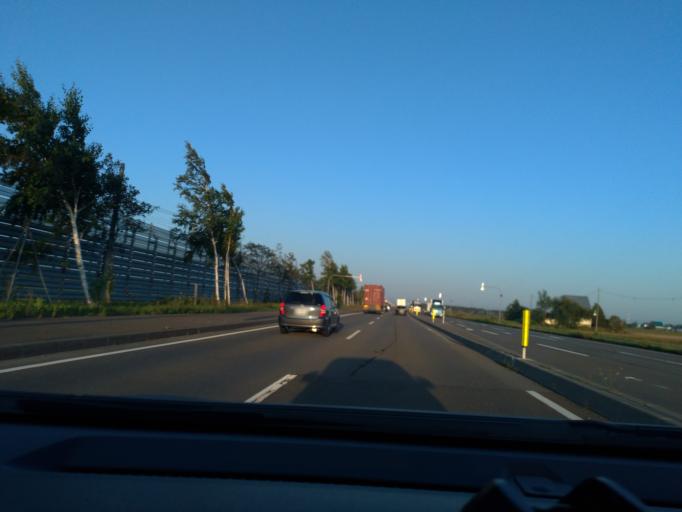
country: JP
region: Hokkaido
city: Tobetsu
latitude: 43.1793
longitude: 141.4638
